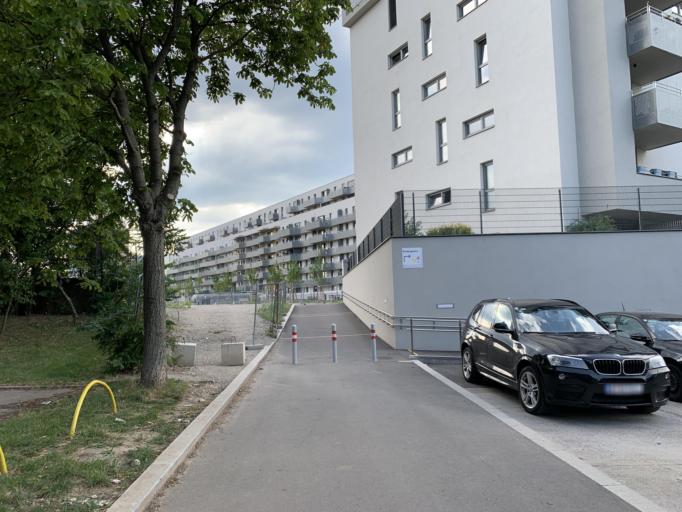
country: AT
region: Vienna
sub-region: Wien Stadt
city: Vienna
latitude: 48.1695
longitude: 16.3570
